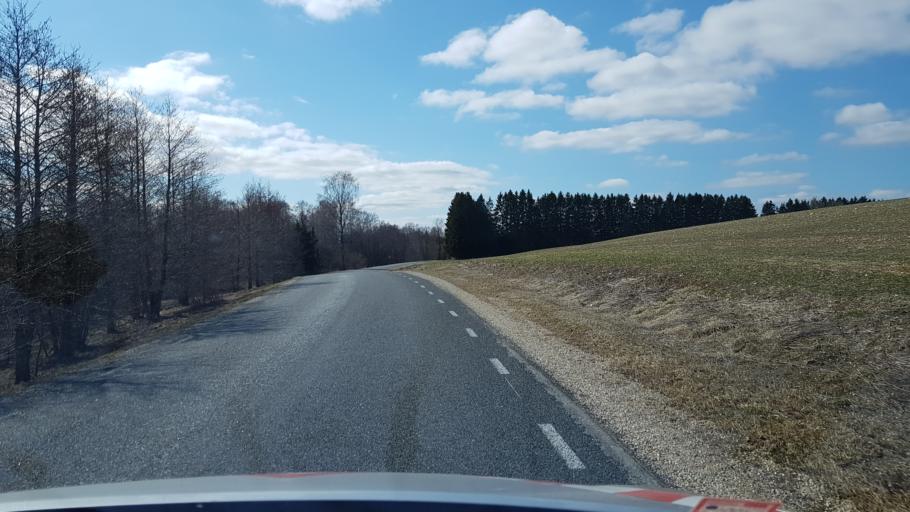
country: EE
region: Laeaene-Virumaa
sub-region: Tapa vald
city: Tapa
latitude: 59.2487
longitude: 25.6961
